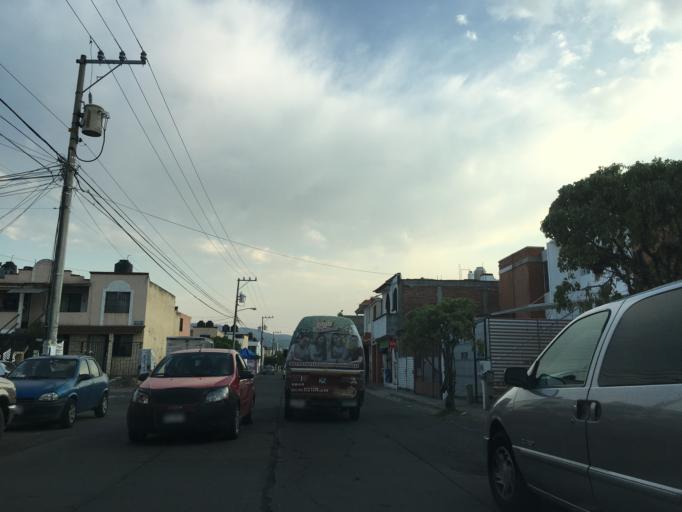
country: MX
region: Michoacan
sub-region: Morelia
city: Morelos
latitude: 19.6740
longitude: -101.2300
